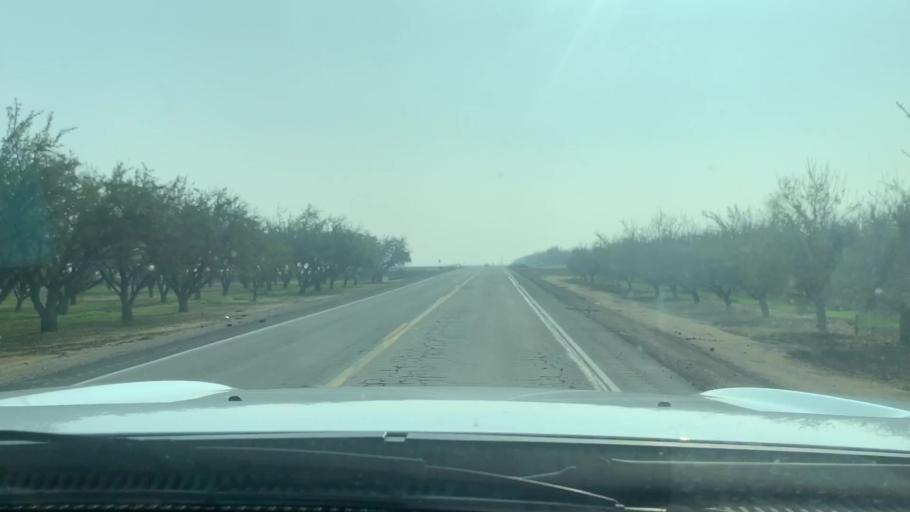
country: US
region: California
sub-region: Kern County
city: Rosedale
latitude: 35.4756
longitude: -119.1533
